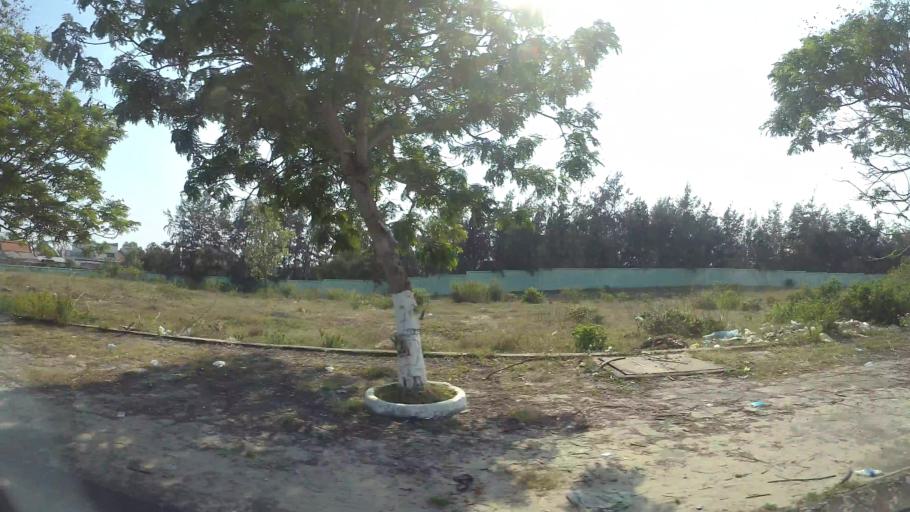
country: VN
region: Da Nang
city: Ngu Hanh Son
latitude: 15.9584
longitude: 108.2909
